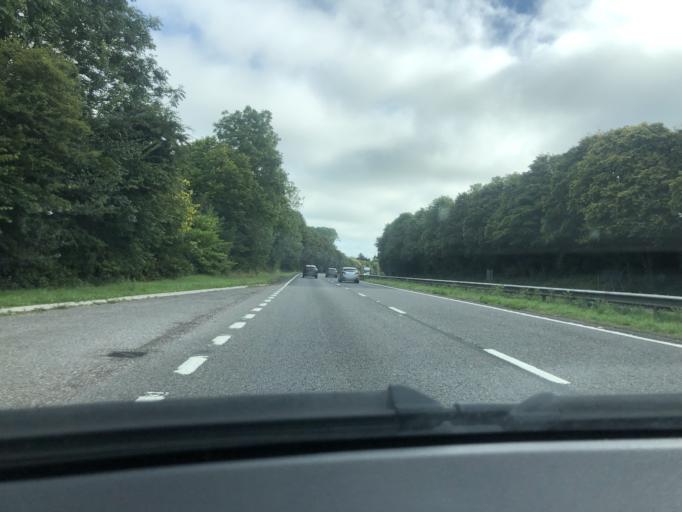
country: GB
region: England
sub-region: Devon
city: Honiton
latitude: 50.7994
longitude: -3.2040
